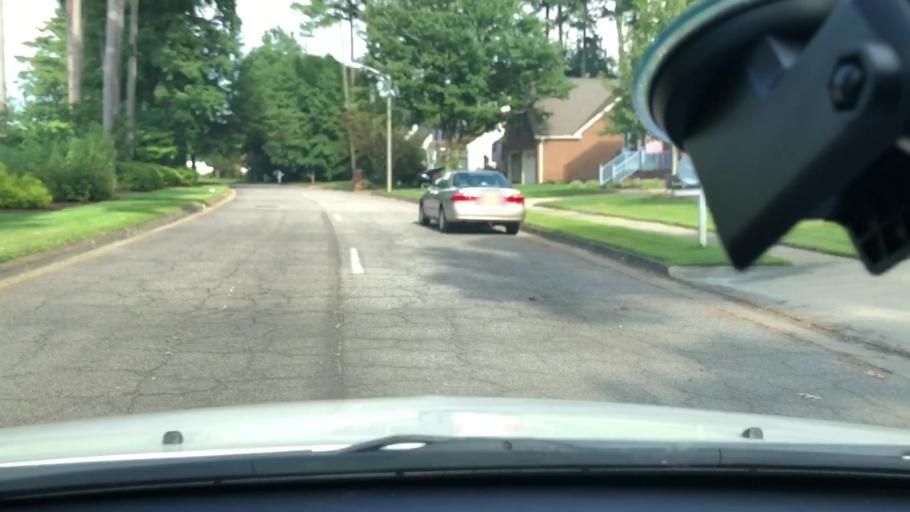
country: US
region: Virginia
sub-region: City of Chesapeake
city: Chesapeake
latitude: 36.7090
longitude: -76.2816
